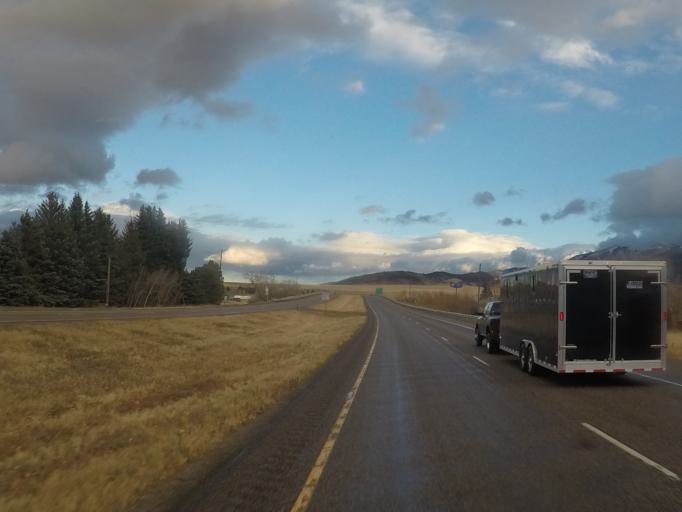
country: US
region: Montana
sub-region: Park County
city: Livingston
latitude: 45.6444
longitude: -110.5795
